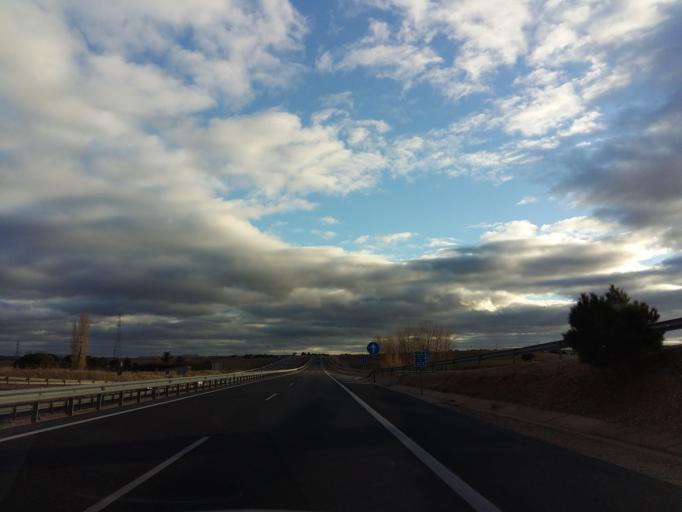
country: ES
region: Castille and Leon
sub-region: Provincia de Burgos
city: Cogollos
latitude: 42.2237
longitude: -3.7044
